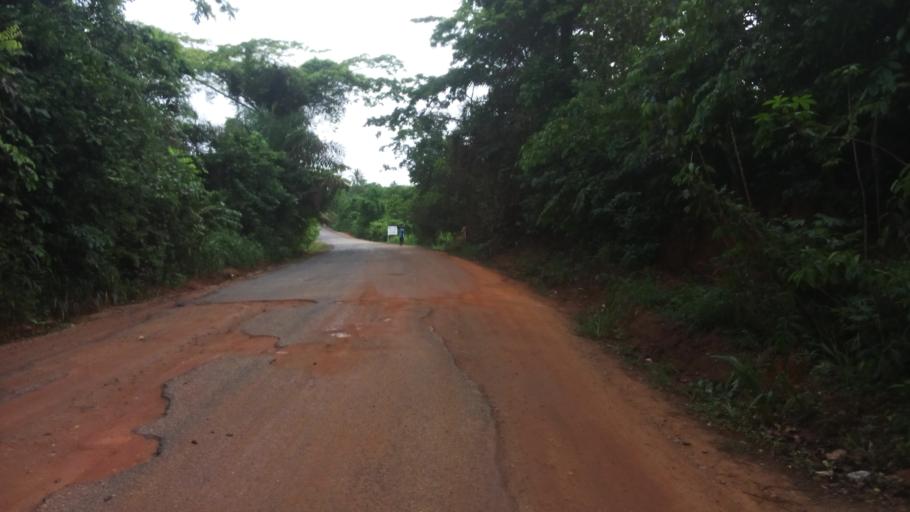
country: GH
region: Central
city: Swedru
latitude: 5.6574
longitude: -0.7549
